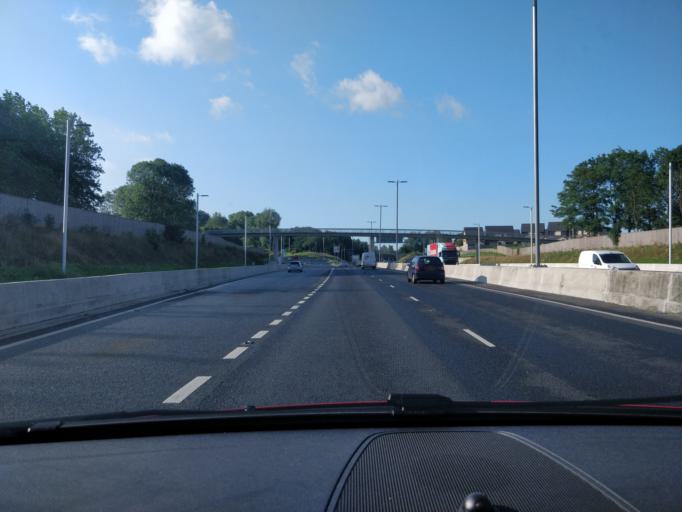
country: GB
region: England
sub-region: Borough of Halton
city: Halton
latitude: 53.3337
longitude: -2.7040
